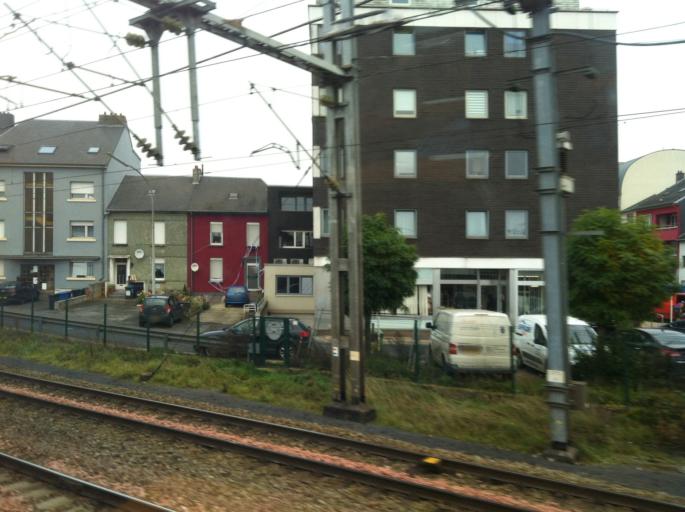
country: LU
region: Luxembourg
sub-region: Canton d'Esch-sur-Alzette
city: Bettembourg
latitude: 49.5177
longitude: 6.1019
